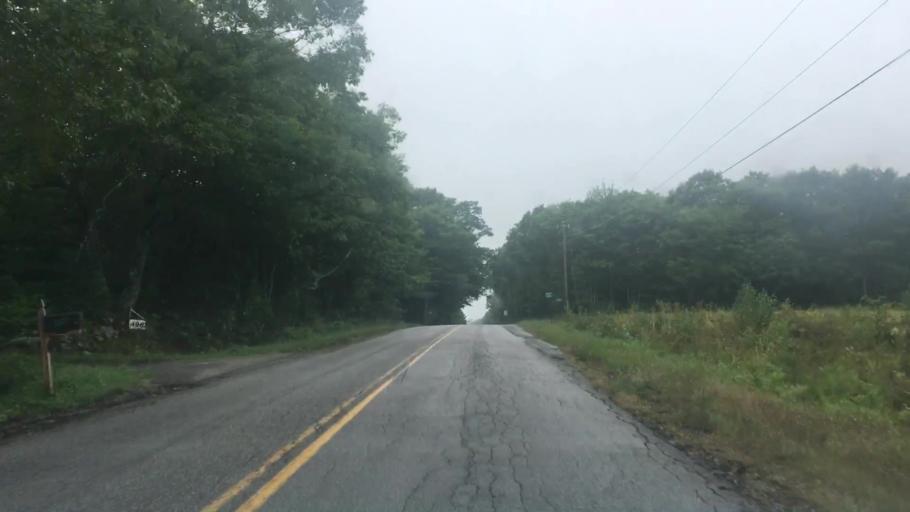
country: US
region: Maine
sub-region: Waldo County
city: Stockton Springs
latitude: 44.5410
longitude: -68.9138
